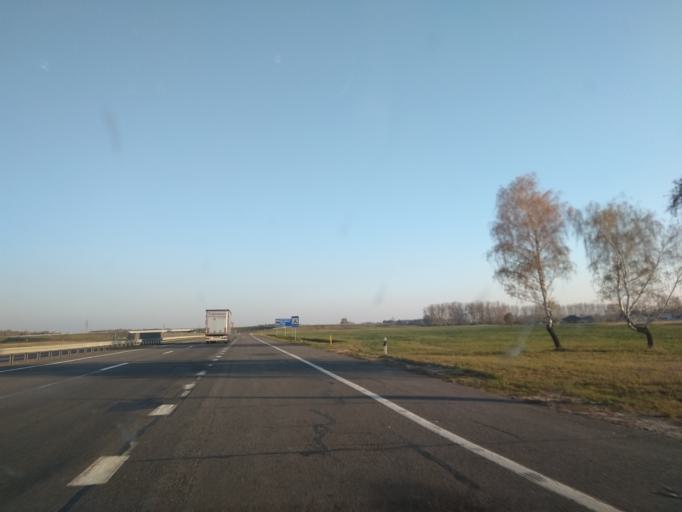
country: BY
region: Brest
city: Kobryn
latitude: 52.1850
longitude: 24.3207
